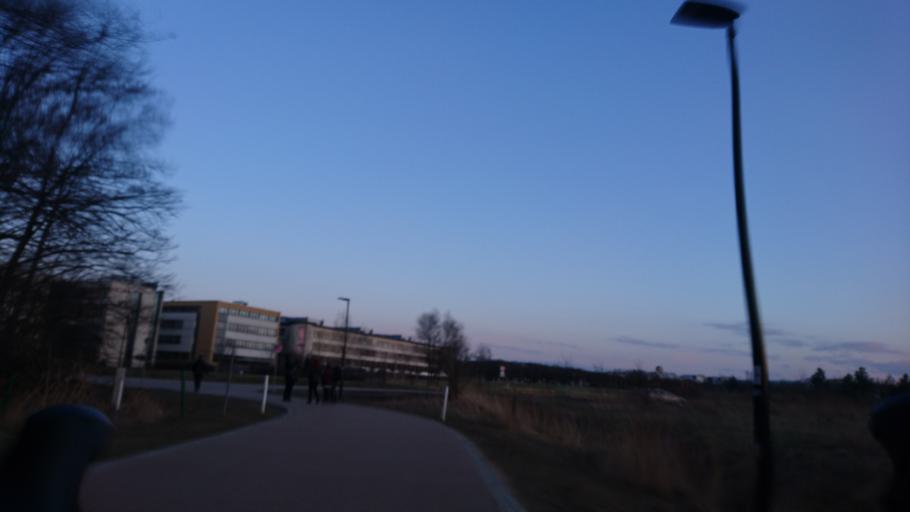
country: PL
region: Lesser Poland Voivodeship
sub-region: Krakow
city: Sidzina
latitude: 50.0280
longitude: 19.8987
